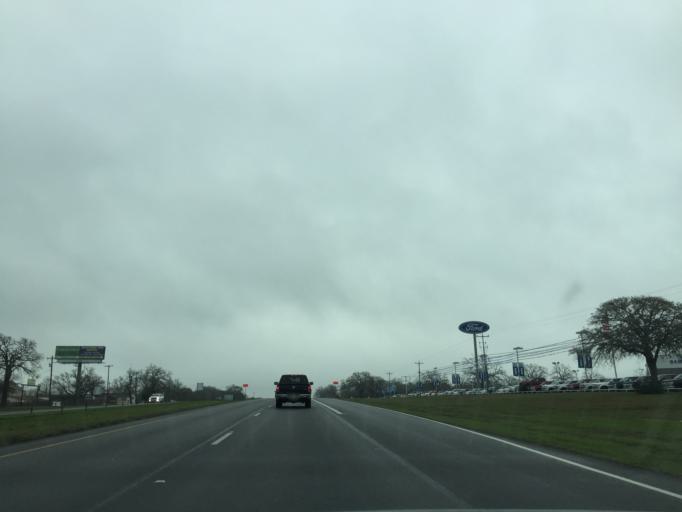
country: US
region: Texas
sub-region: Bastrop County
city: Wyldwood
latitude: 30.1103
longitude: -97.4063
